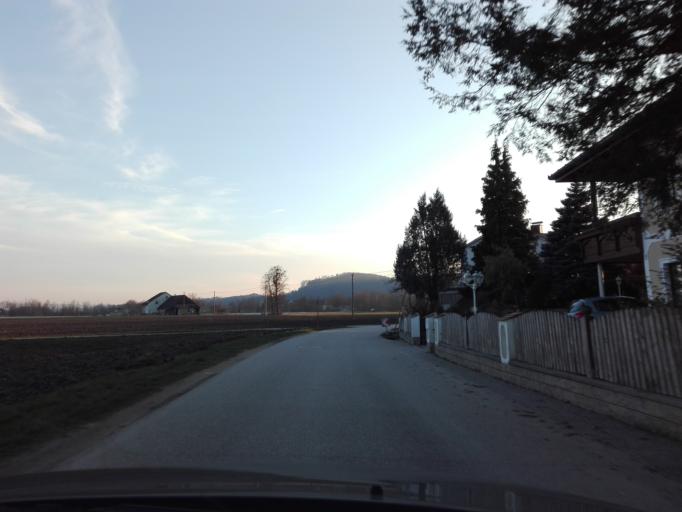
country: AT
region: Upper Austria
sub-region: Politischer Bezirk Urfahr-Umgebung
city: Feldkirchen an der Donau
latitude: 48.3466
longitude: 14.0068
